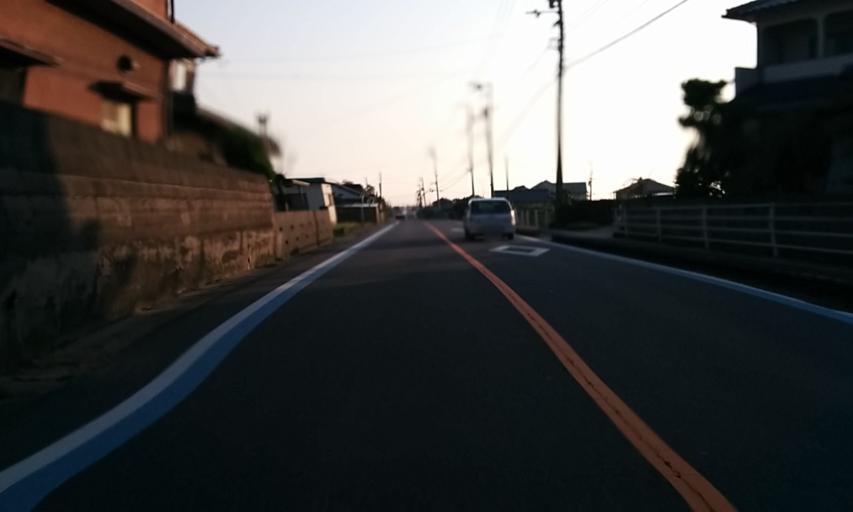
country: JP
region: Ehime
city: Masaki-cho
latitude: 33.7770
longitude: 132.7531
